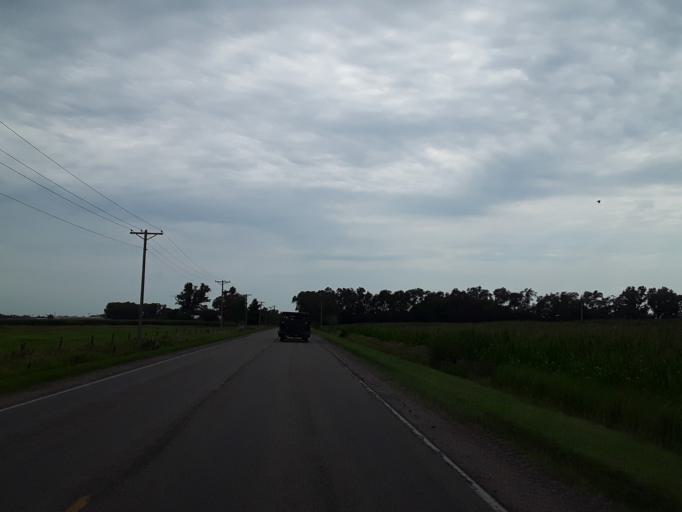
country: US
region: Nebraska
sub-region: Saunders County
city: Yutan
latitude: 41.2448
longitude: -96.3304
